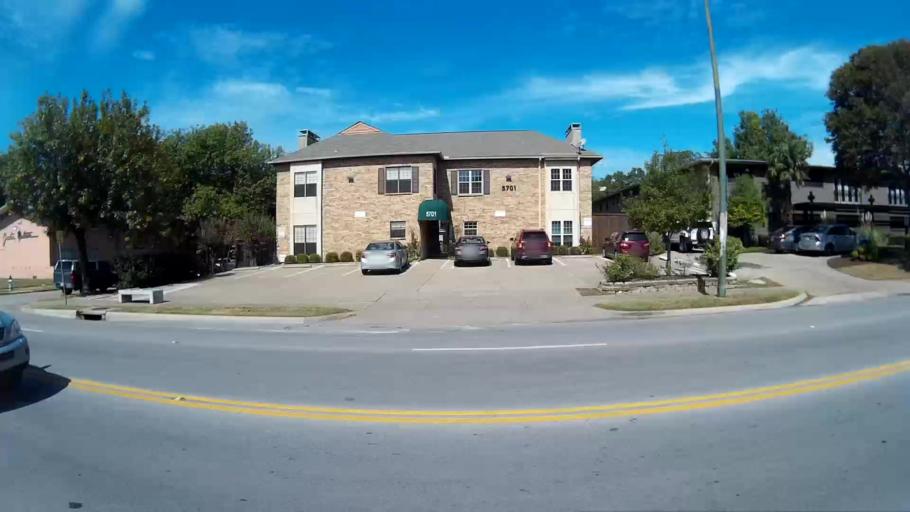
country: US
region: Texas
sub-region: Dallas County
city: Highland Park
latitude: 32.8076
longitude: -96.7602
